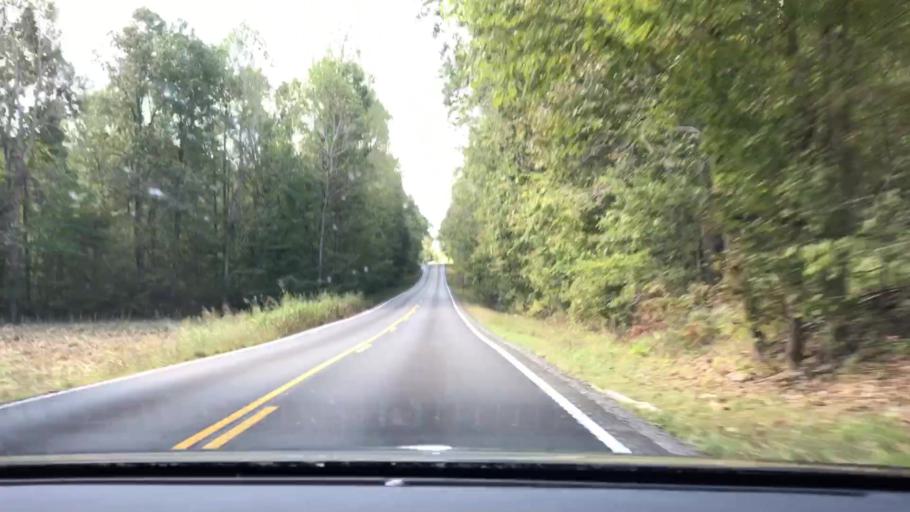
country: US
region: Kentucky
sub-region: Graves County
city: Mayfield
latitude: 36.8736
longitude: -88.5684
